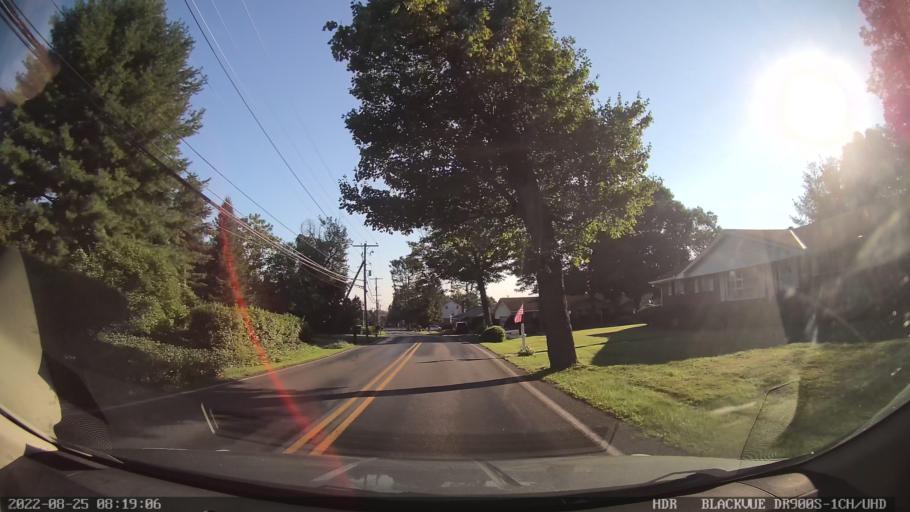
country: US
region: Pennsylvania
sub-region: Lehigh County
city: Wescosville
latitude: 40.5597
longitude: -75.5341
